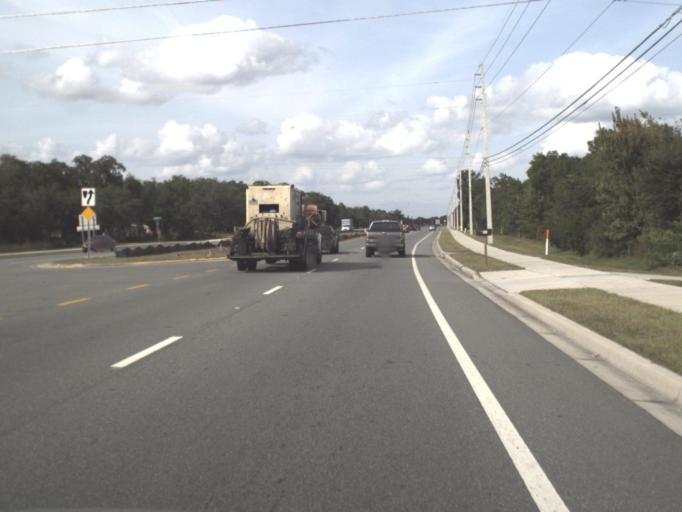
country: US
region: Florida
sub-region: Osceola County
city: Saint Cloud
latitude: 28.2791
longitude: -81.2437
